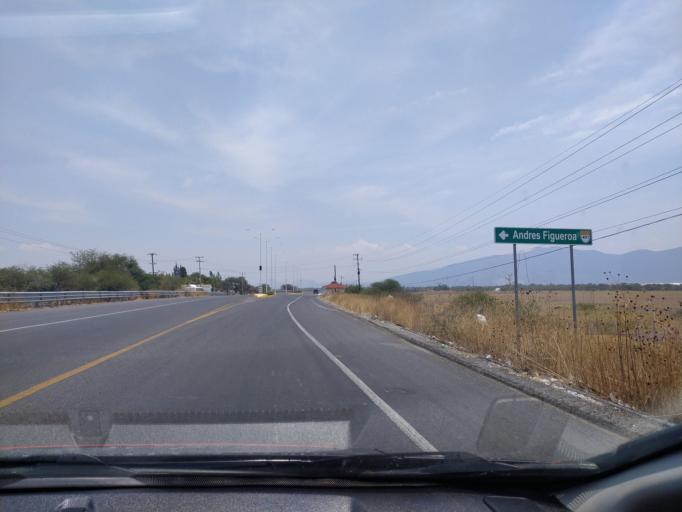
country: MX
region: Jalisco
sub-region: Zacoalco de Torres
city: Barranca de Otates (Barranca de Otatan)
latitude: 20.2940
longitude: -103.6015
